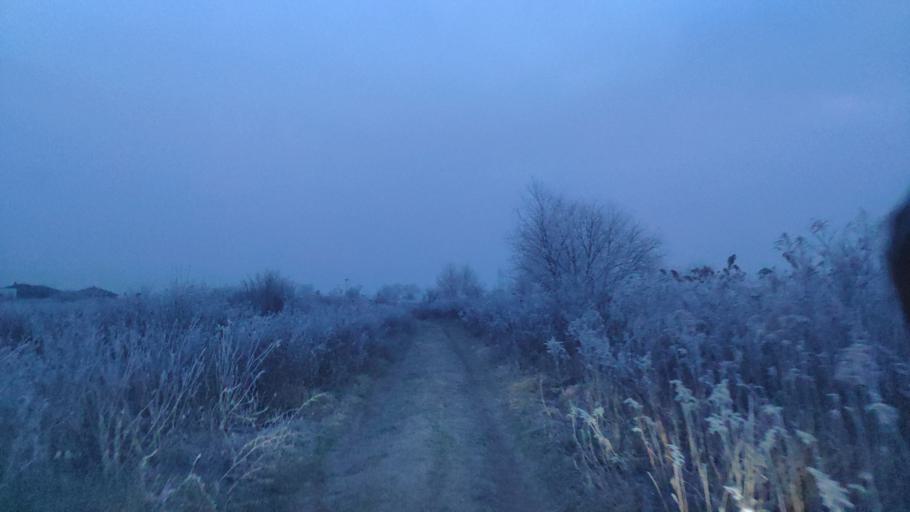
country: SK
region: Kosicky
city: Kosice
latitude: 48.6150
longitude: 21.3353
